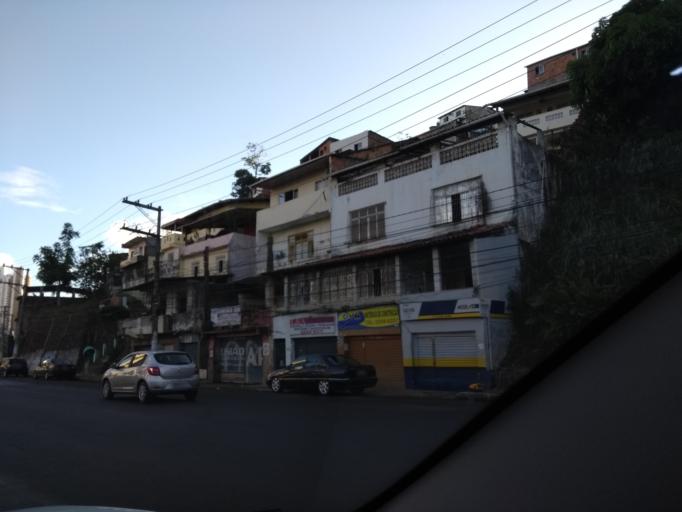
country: BR
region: Bahia
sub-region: Salvador
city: Salvador
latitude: -12.9989
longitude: -38.4922
